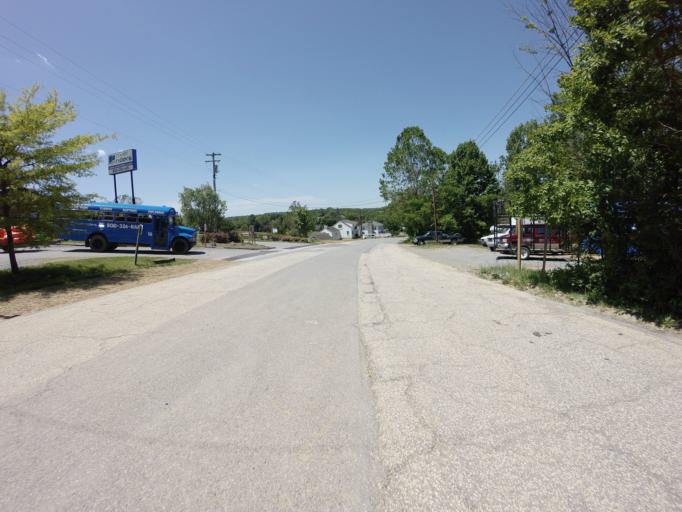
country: US
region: West Virginia
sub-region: Jefferson County
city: Bolivar
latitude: 39.3165
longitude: -77.7688
